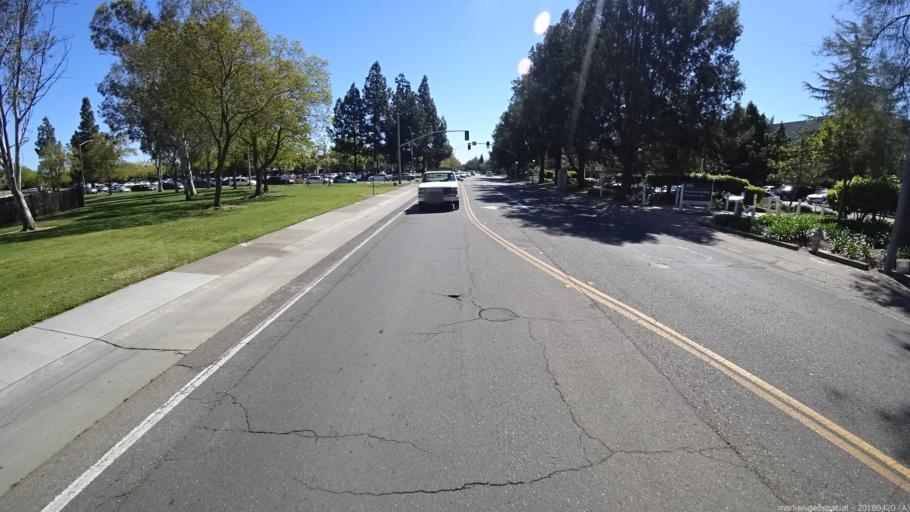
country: US
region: California
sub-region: Sacramento County
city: Parkway
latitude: 38.5468
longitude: -121.4473
